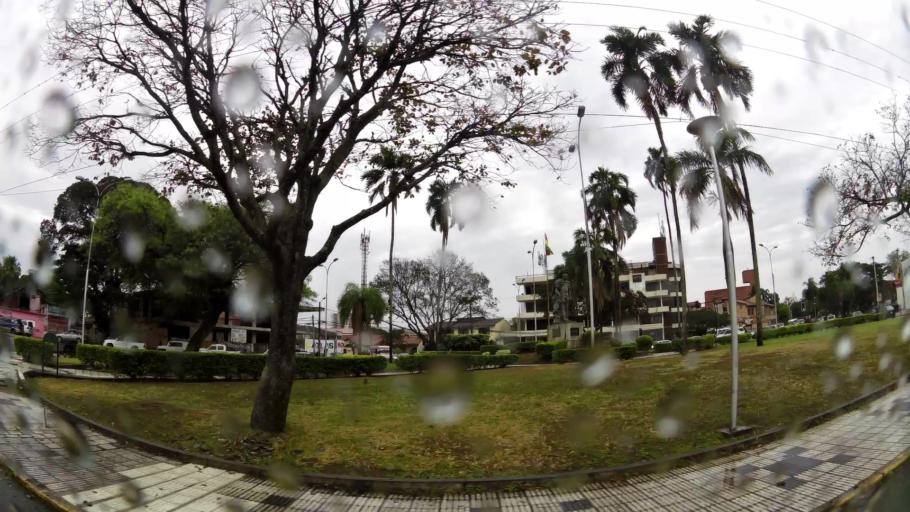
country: BO
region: Santa Cruz
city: Santa Cruz de la Sierra
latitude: -17.7911
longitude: -63.1732
